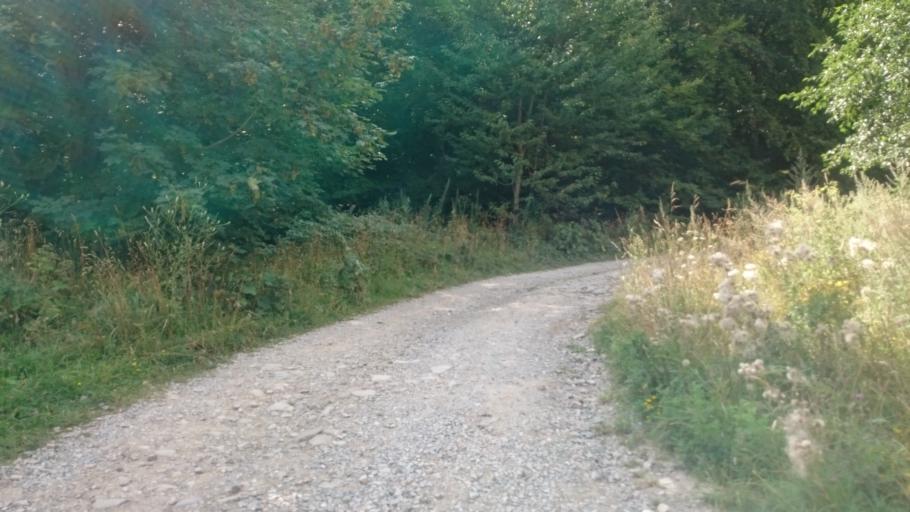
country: IT
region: Emilia-Romagna
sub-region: Provincia di Reggio Emilia
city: Villa Minozzo
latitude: 44.2979
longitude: 10.4273
